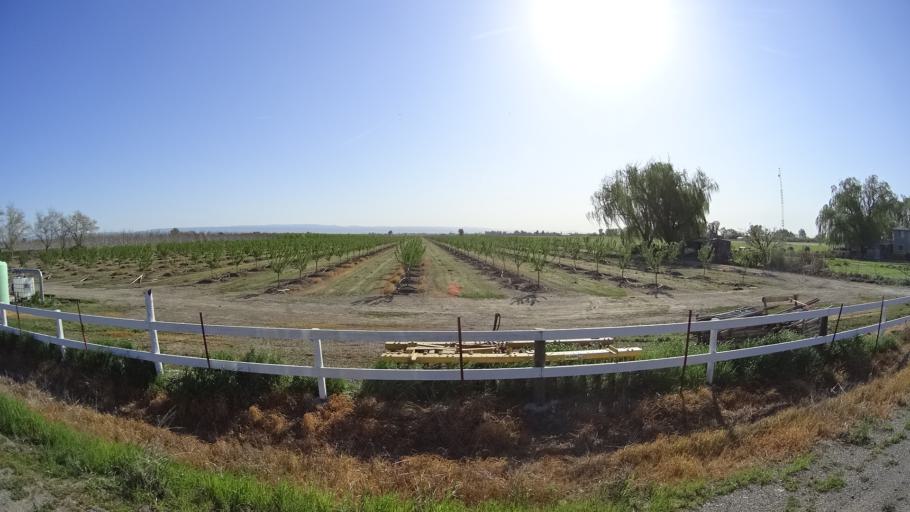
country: US
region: California
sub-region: Glenn County
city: Orland
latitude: 39.8009
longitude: -122.1041
